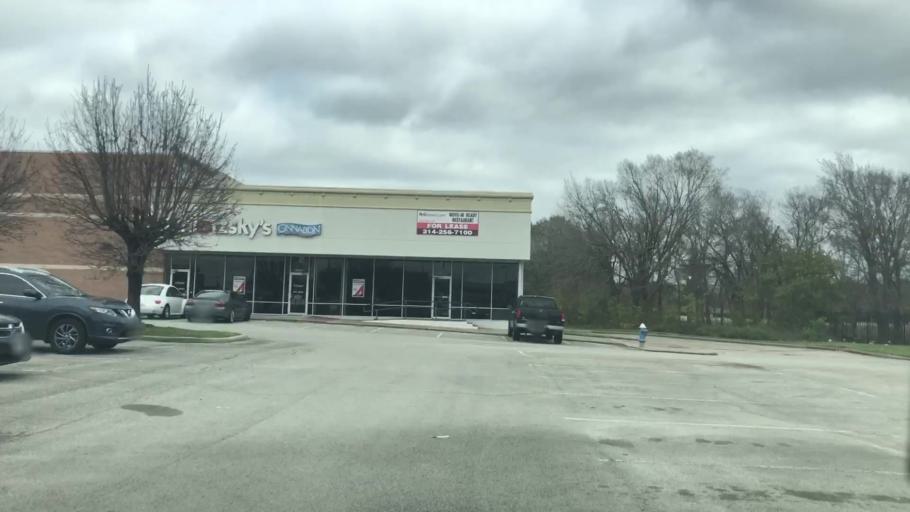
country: US
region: Texas
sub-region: Harris County
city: Hudson
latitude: 29.8482
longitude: -95.5012
